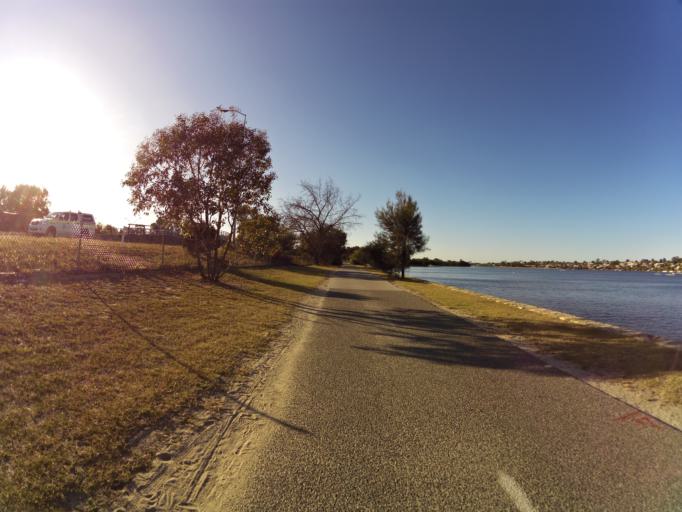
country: AU
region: Western Australia
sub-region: South Perth
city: Manning
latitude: -32.0124
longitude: 115.8565
